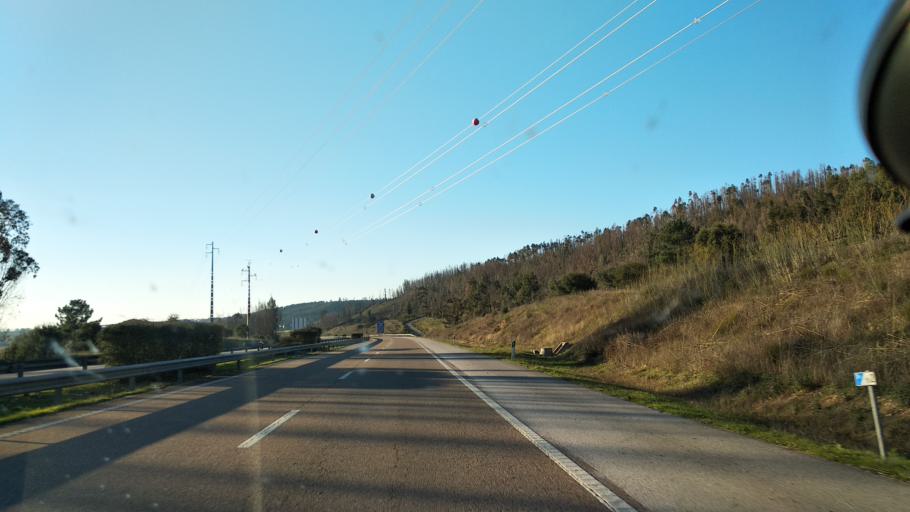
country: PT
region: Santarem
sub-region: Abrantes
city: Tramagal
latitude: 39.4838
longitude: -8.2480
